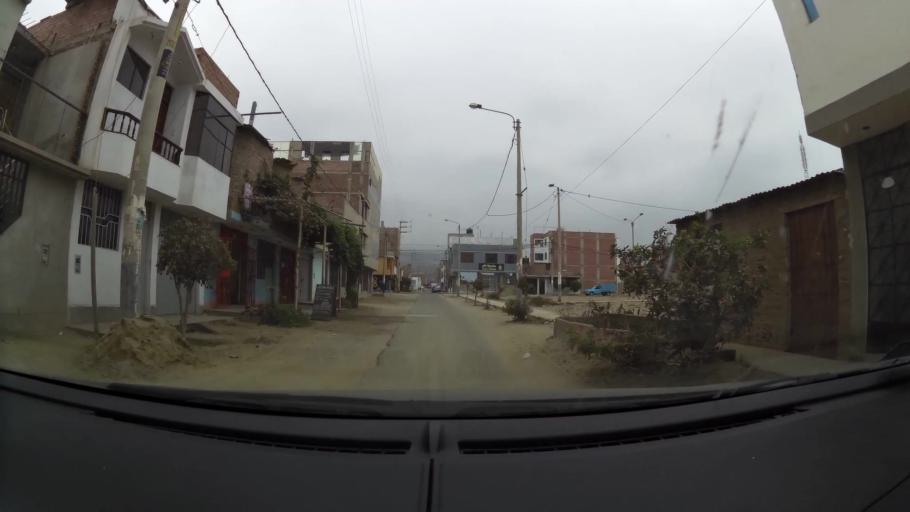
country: PE
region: La Libertad
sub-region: Provincia de Trujillo
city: La Esperanza
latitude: -8.0895
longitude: -79.0440
